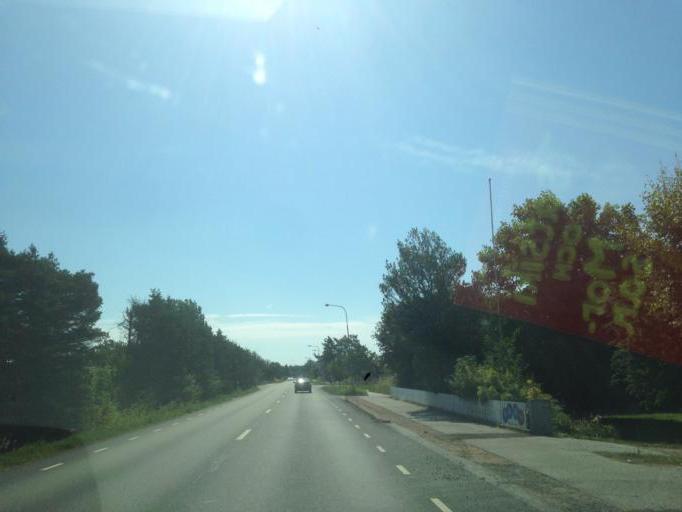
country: SE
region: Skane
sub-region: Simrishamns Kommun
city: Kivik
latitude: 55.6167
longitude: 14.2799
